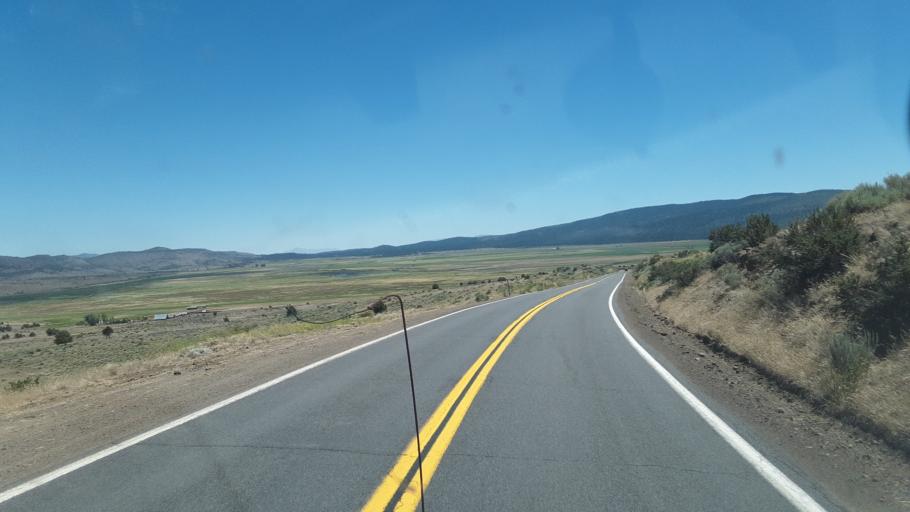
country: US
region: California
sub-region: Lassen County
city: Susanville
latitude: 40.5908
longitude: -120.6422
